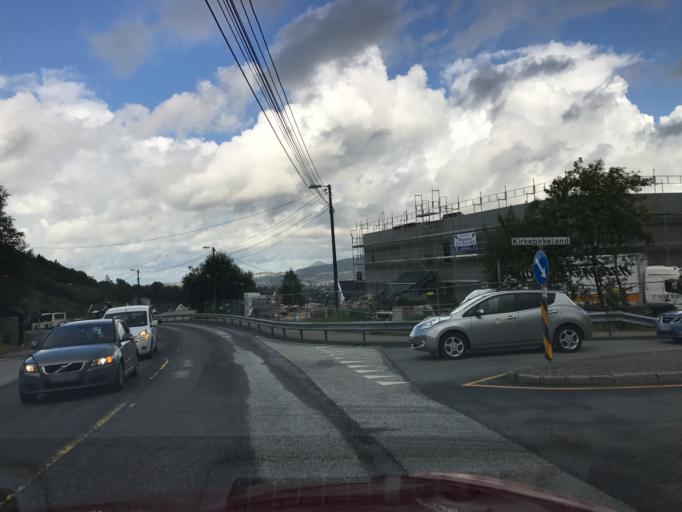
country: NO
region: Hordaland
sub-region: Bergen
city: Sandsli
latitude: 60.2999
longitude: 5.3787
